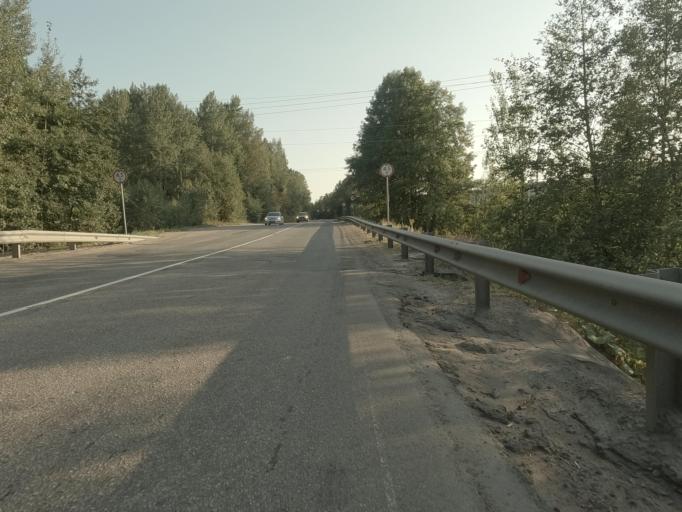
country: RU
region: Leningrad
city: Vyborg
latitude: 60.7402
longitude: 28.7627
